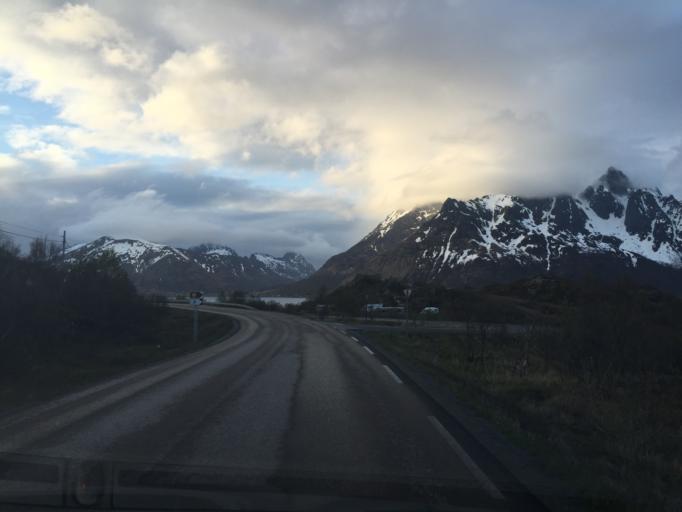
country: NO
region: Nordland
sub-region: Vagan
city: Svolvaer
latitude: 68.3145
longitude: 14.7137
